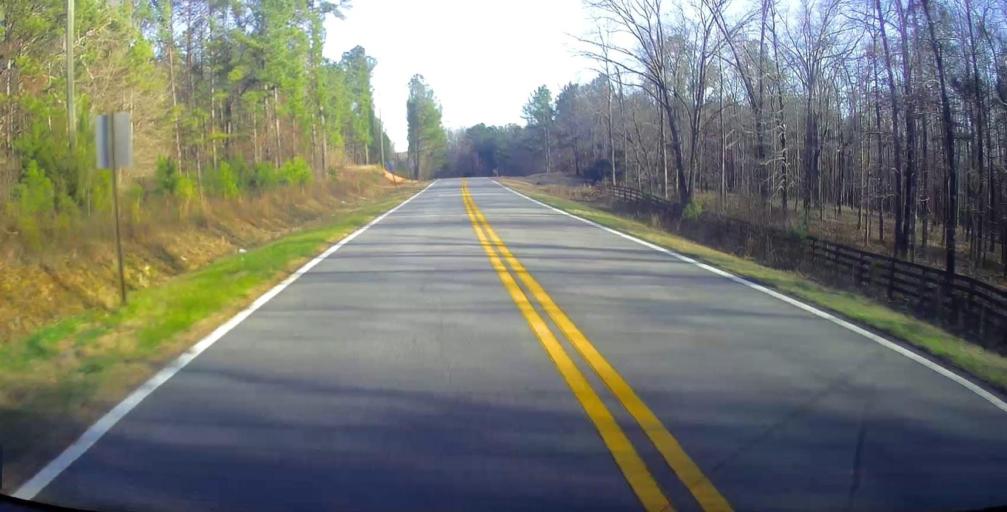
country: US
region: Georgia
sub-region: Bibb County
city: West Point
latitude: 32.8341
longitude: -83.8942
